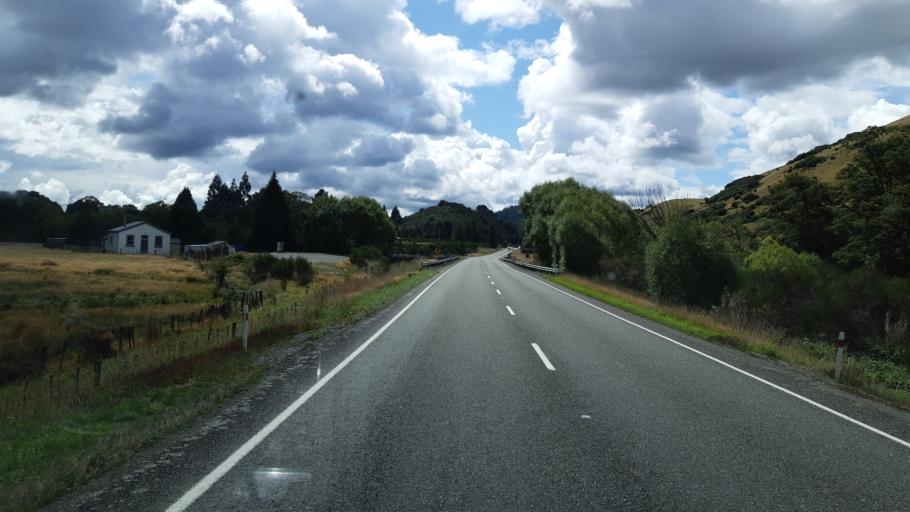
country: NZ
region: Tasman
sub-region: Tasman District
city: Wakefield
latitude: -41.6500
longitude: 172.6493
